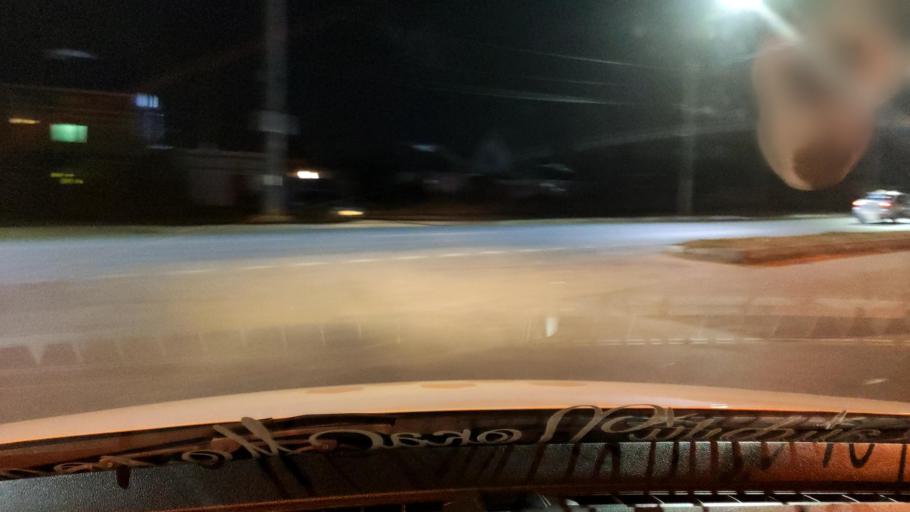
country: RU
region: Voronezj
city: Voronezh
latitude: 51.6371
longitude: 39.1733
